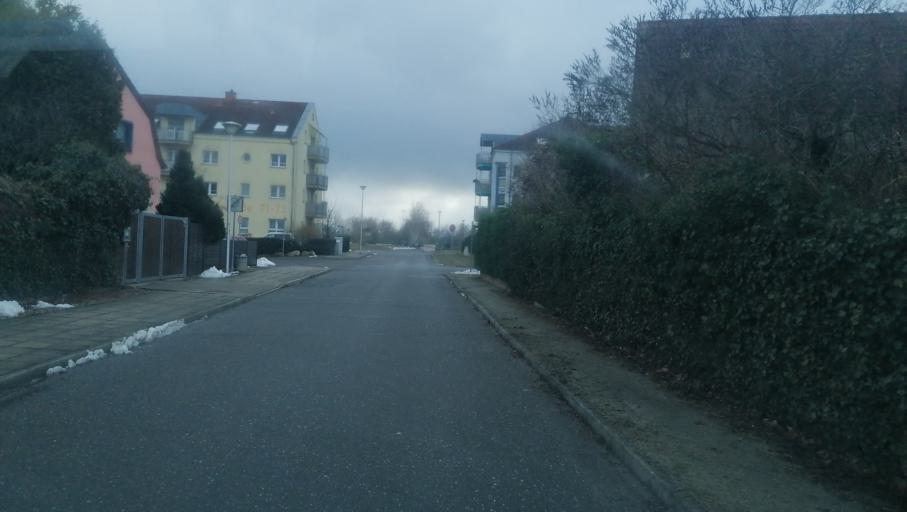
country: DE
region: Brandenburg
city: Cottbus
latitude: 51.7221
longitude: 14.3298
